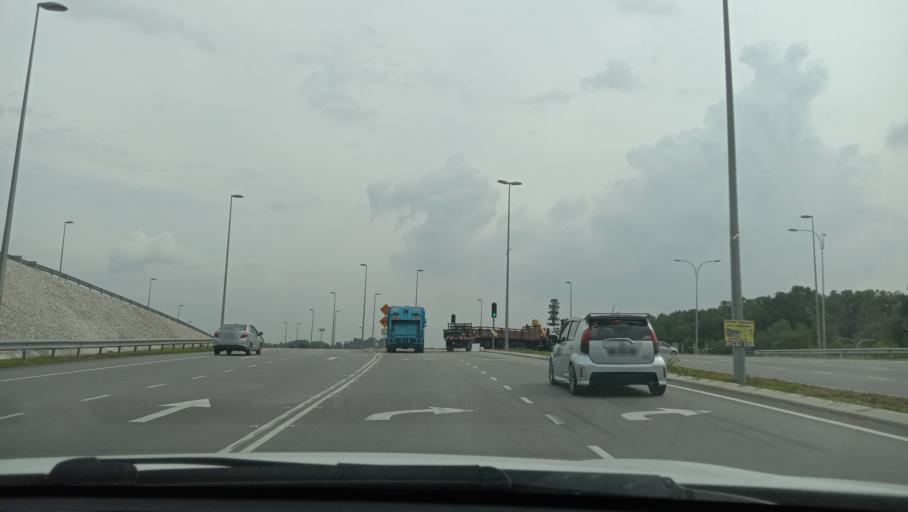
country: MY
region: Selangor
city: Kampung Baru Subang
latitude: 3.1277
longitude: 101.5263
